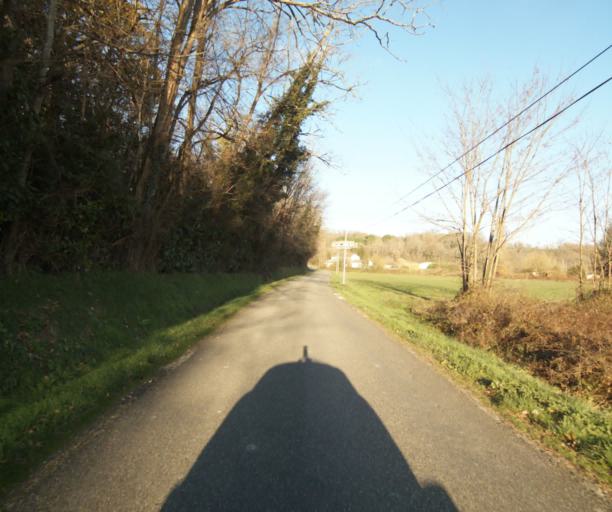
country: FR
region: Midi-Pyrenees
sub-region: Departement du Tarn-et-Garonne
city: Moissac
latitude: 44.1225
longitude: 1.1297
